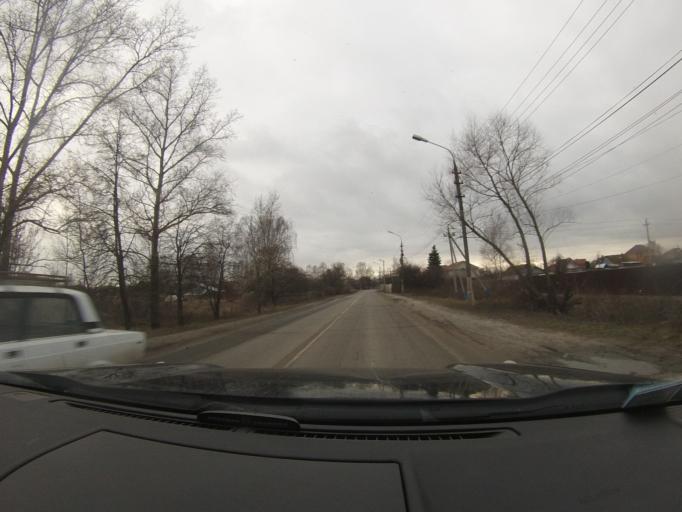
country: RU
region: Moskovskaya
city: Lopatinskiy
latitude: 55.3260
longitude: 38.7019
